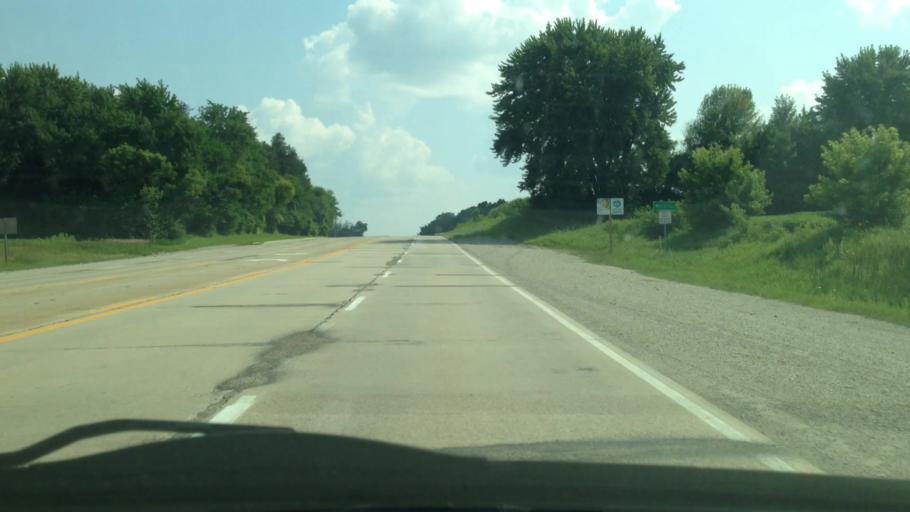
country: US
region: Iowa
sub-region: Black Hawk County
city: Waterloo
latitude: 42.5641
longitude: -92.3377
